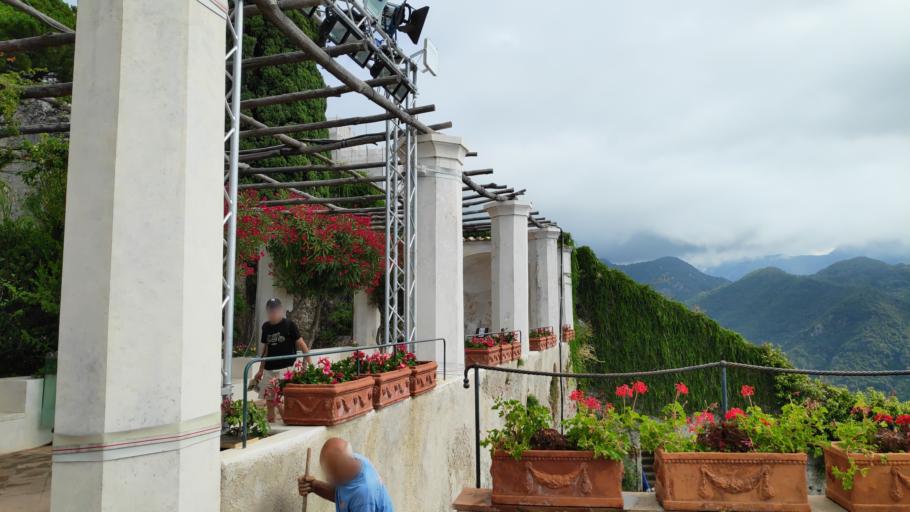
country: IT
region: Campania
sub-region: Provincia di Salerno
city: Ravello
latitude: 40.6487
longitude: 14.6132
